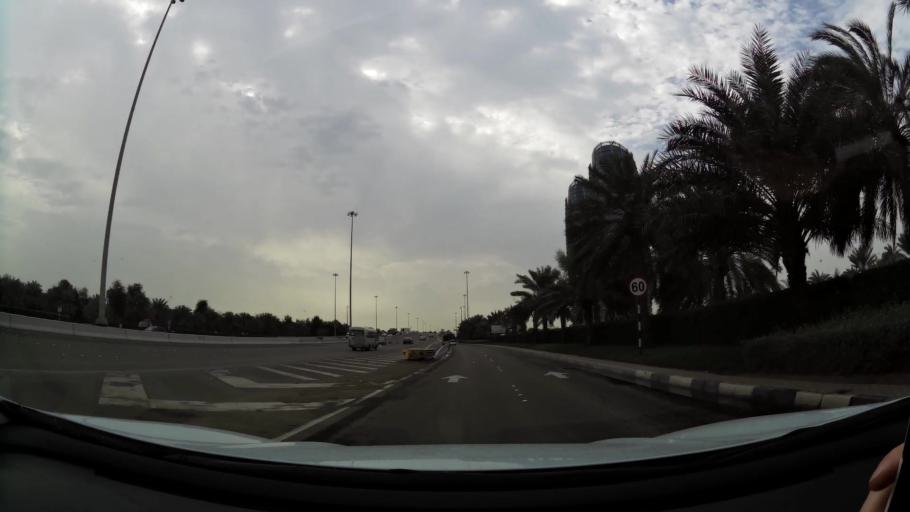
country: AE
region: Abu Dhabi
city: Abu Dhabi
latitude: 24.4594
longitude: 54.4003
